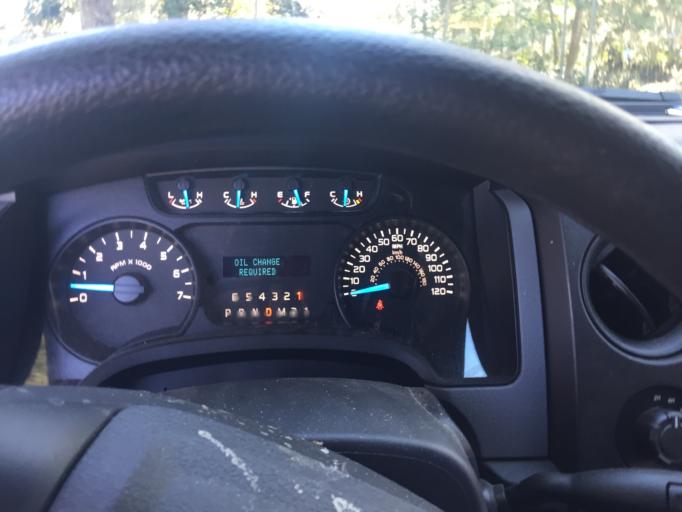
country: US
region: Georgia
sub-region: Chatham County
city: Thunderbolt
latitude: 32.0122
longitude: -81.0651
